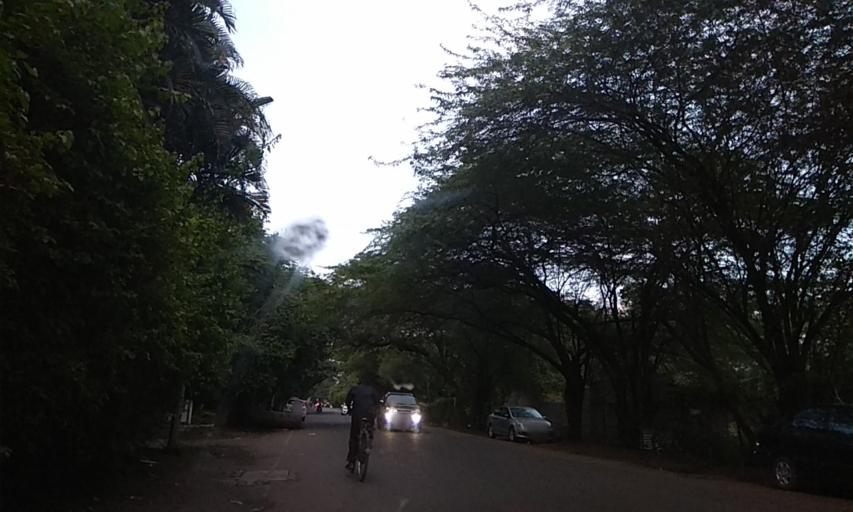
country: IN
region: Maharashtra
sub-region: Pune Division
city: Pune
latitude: 18.5069
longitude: 73.9089
